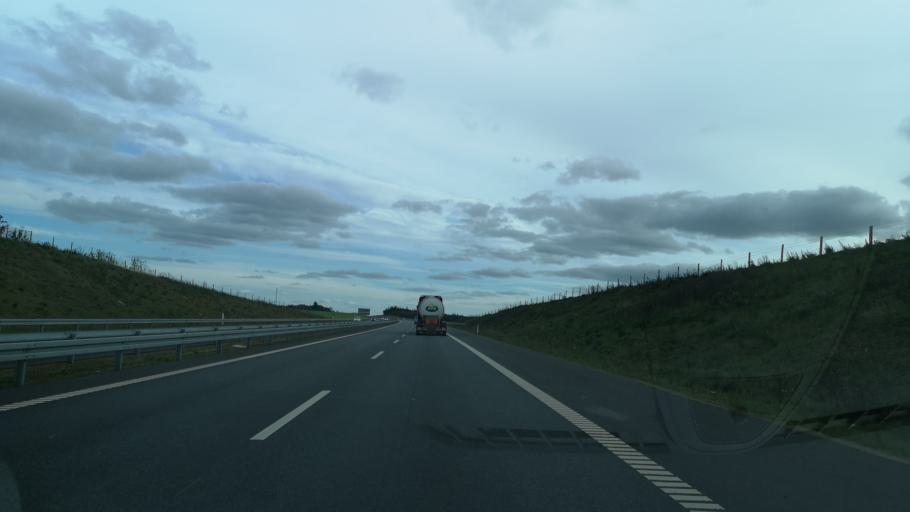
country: DK
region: Central Jutland
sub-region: Herning Kommune
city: Avlum
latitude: 56.2785
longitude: 8.7410
